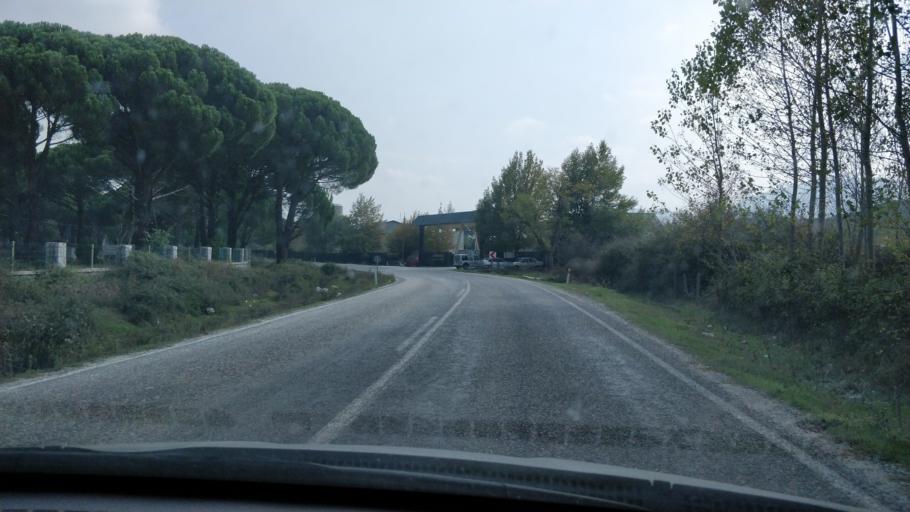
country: TR
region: Izmir
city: Kozak
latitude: 39.2592
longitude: 27.0385
